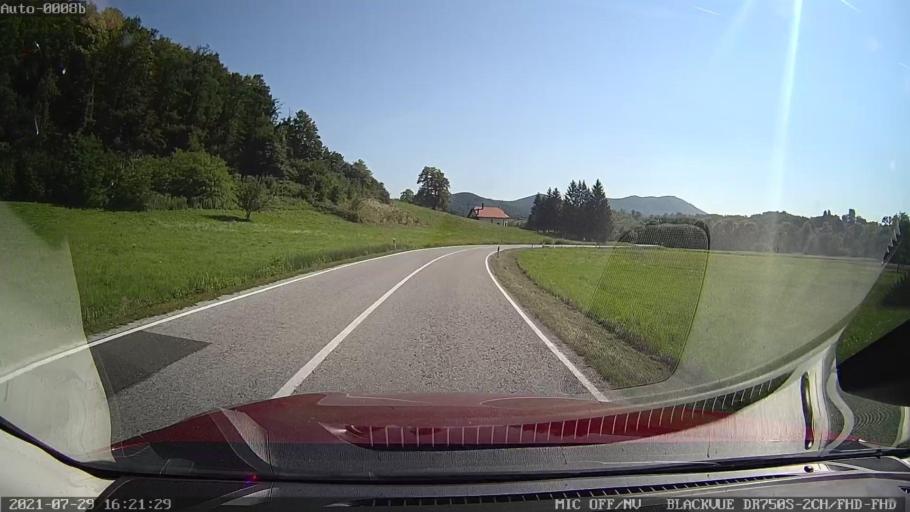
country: HR
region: Varazdinska
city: Lepoglava
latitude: 46.2341
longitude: 15.9676
